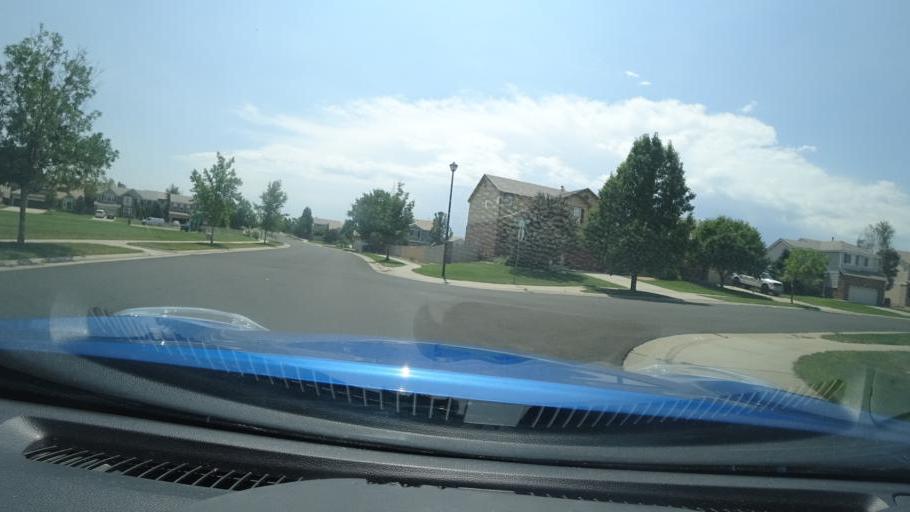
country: US
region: Colorado
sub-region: Adams County
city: Aurora
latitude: 39.6728
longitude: -104.7691
